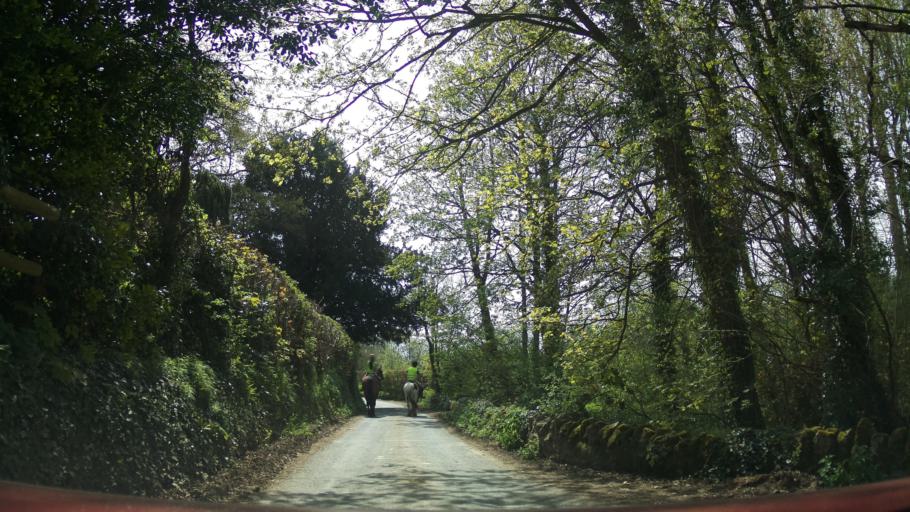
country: GB
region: England
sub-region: Dorset
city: Sherborne
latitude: 50.9881
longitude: -2.5400
